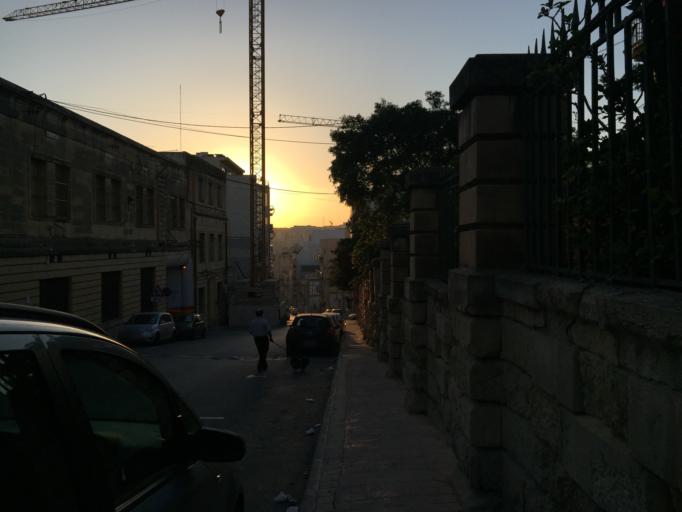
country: MT
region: Tal-Pieta
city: Pieta
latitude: 35.8934
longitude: 14.4935
